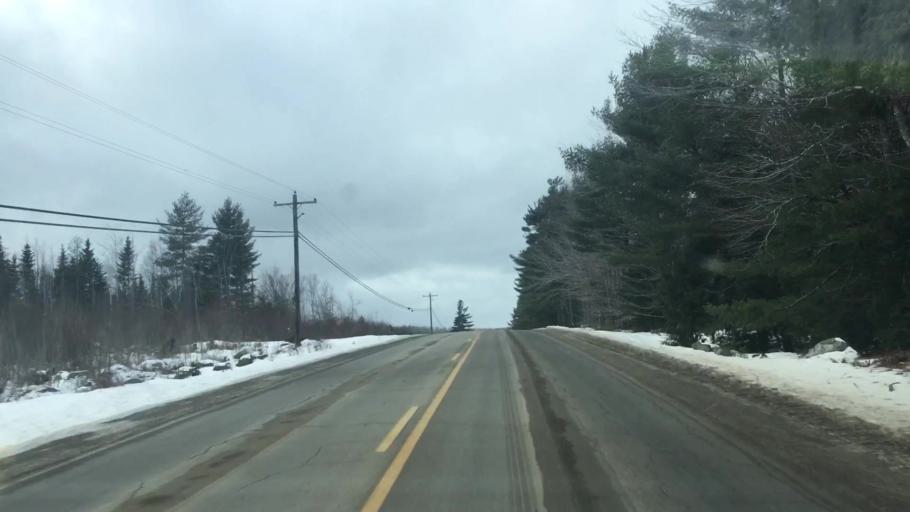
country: US
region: Maine
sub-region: Washington County
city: Calais
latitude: 45.0070
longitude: -67.4101
